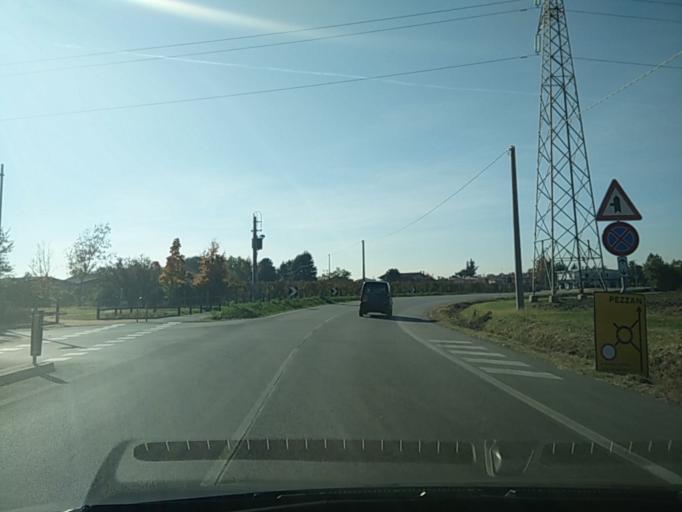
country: IT
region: Veneto
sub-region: Provincia di Treviso
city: Breda
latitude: 45.7131
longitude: 12.3163
